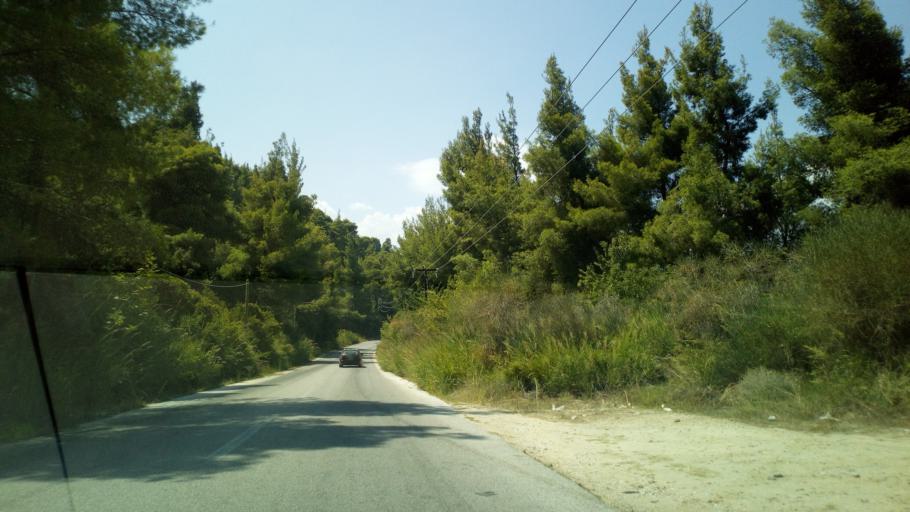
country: GR
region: Central Macedonia
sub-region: Nomos Chalkidikis
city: Neos Marmaras
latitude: 40.1777
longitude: 23.8319
